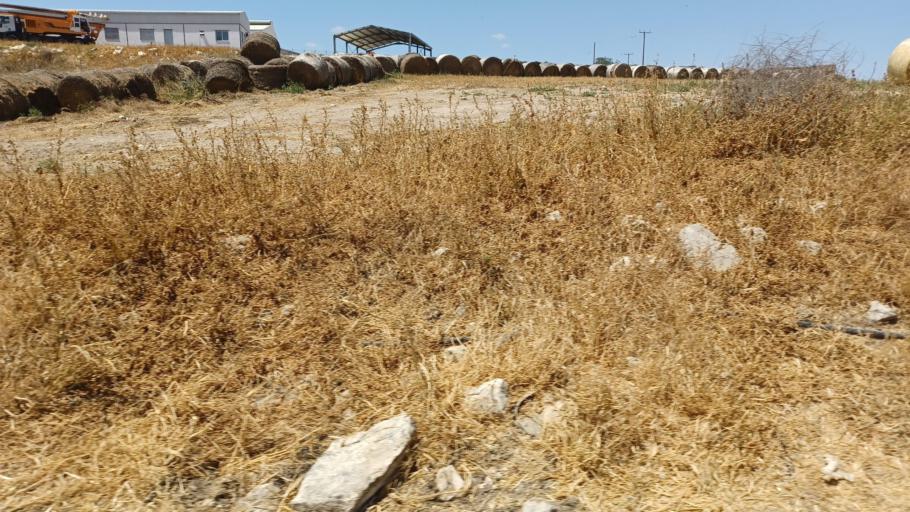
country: CY
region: Larnaka
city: Athienou
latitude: 35.0373
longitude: 33.5434
